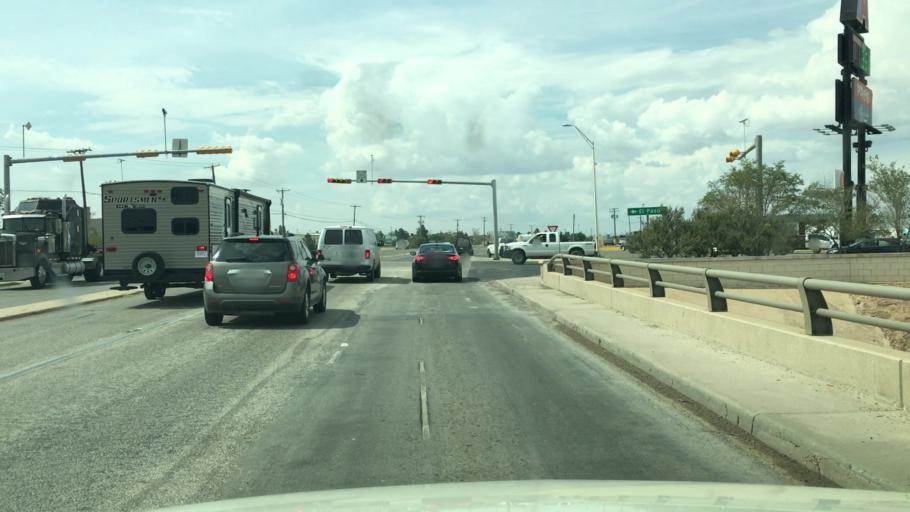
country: US
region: Texas
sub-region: Howard County
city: Big Spring
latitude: 32.2637
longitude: -101.4904
